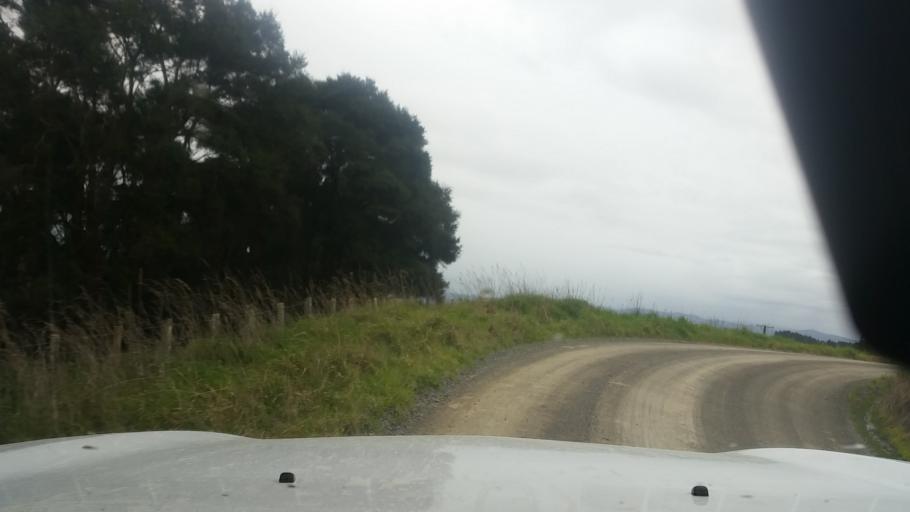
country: NZ
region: Wellington
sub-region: South Wairarapa District
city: Waipawa
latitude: -41.1805
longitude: 175.4783
